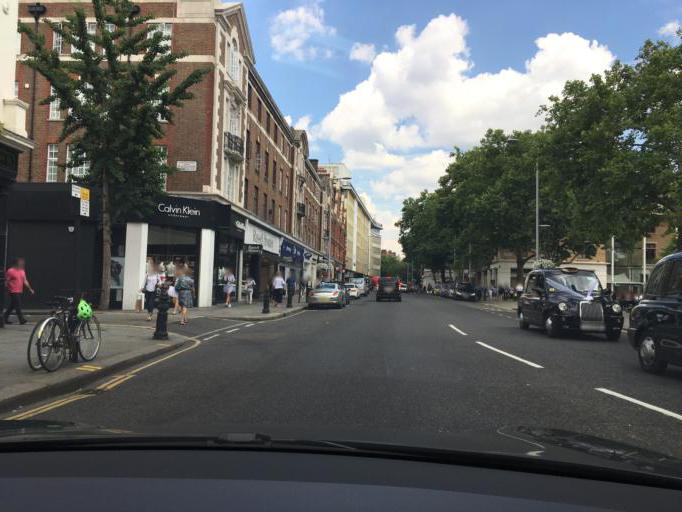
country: GB
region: England
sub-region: Greater London
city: Chelsea
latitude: 51.4910
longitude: -0.1609
